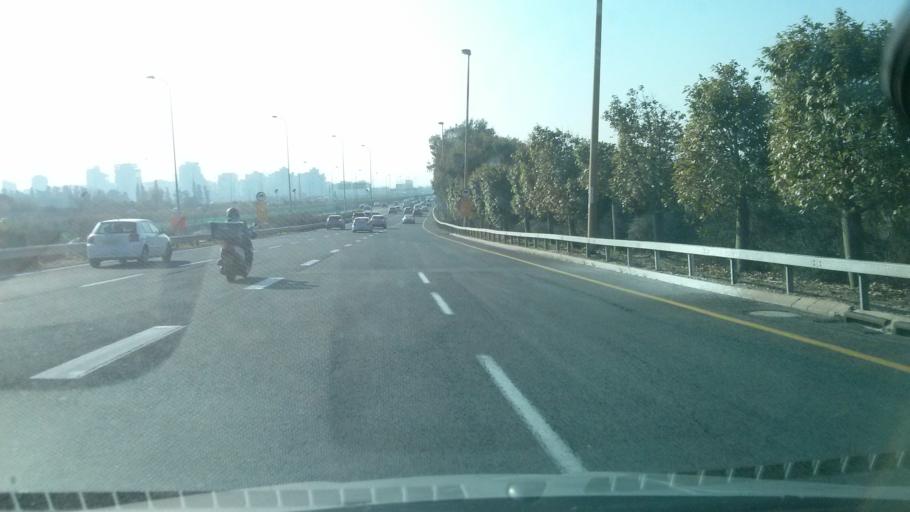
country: IL
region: Tel Aviv
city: Ramat HaSharon
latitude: 32.1373
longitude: 34.8093
